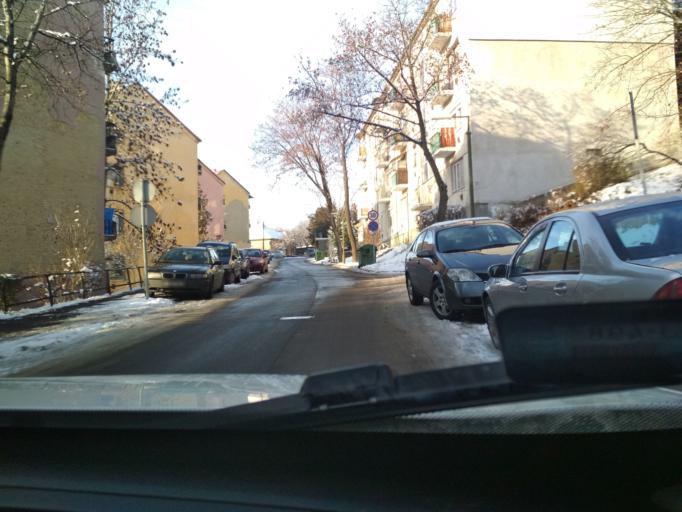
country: HU
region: Nograd
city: Salgotarjan
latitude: 48.1000
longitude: 19.8078
